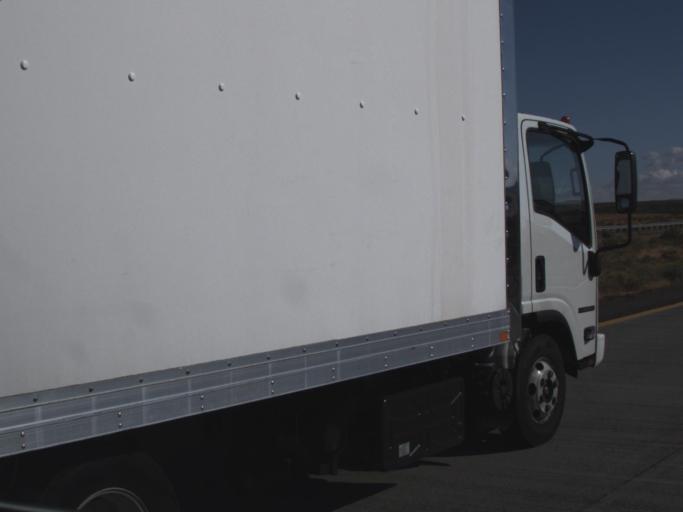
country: US
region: Washington
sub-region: Benton County
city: West Richland
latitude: 46.2161
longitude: -119.3473
